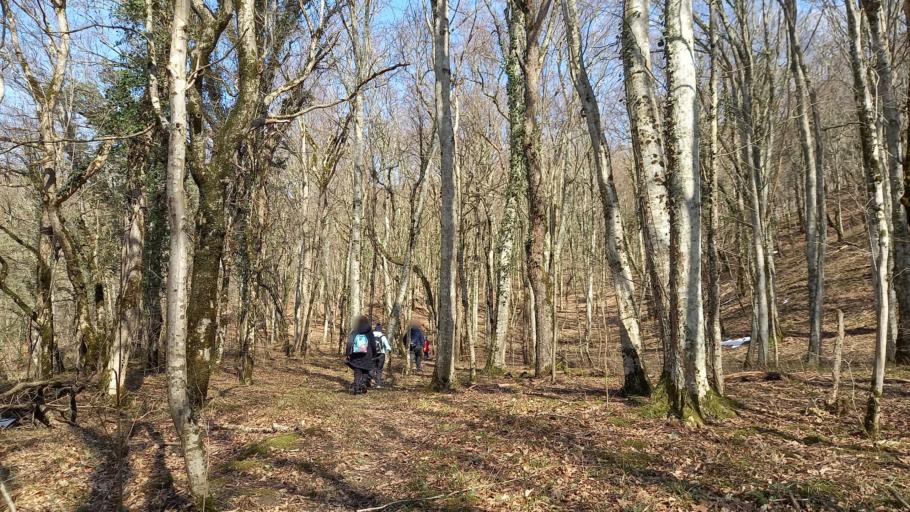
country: RU
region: Krasnodarskiy
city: Arkhipo-Osipovka
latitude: 44.3847
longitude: 38.6043
